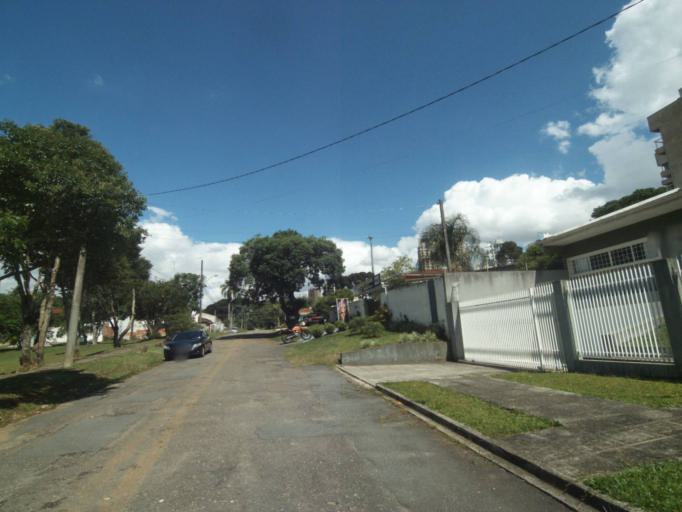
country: BR
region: Parana
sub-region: Curitiba
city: Curitiba
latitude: -25.4351
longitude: -49.3371
